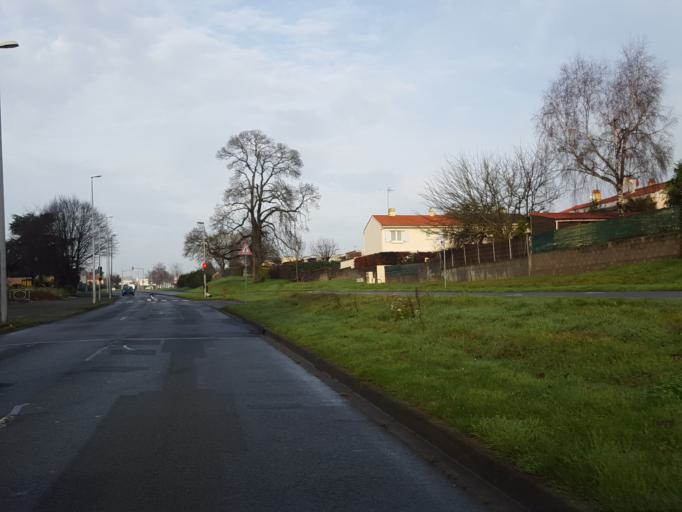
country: FR
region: Pays de la Loire
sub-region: Departement de la Vendee
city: La Roche-sur-Yon
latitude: 46.6814
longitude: -1.4228
